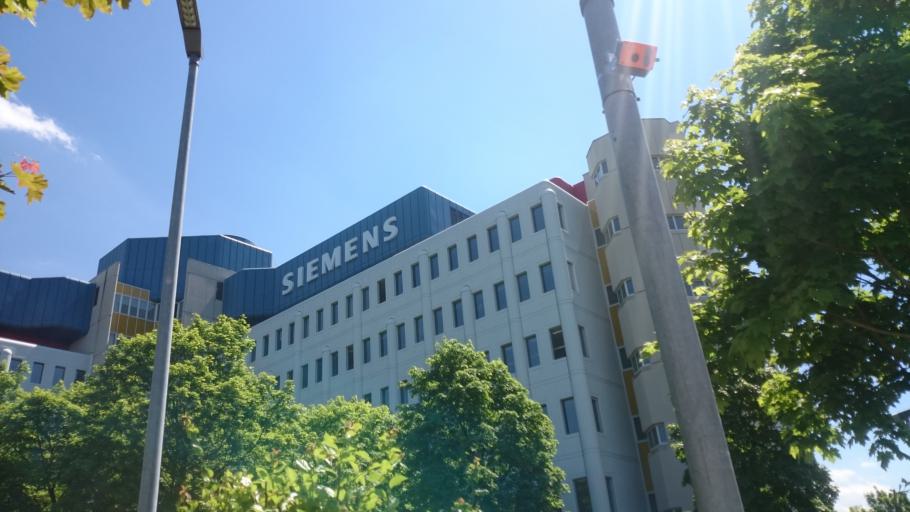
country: DE
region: Bavaria
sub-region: Upper Bavaria
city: Neubiberg
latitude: 48.0918
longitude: 11.6455
